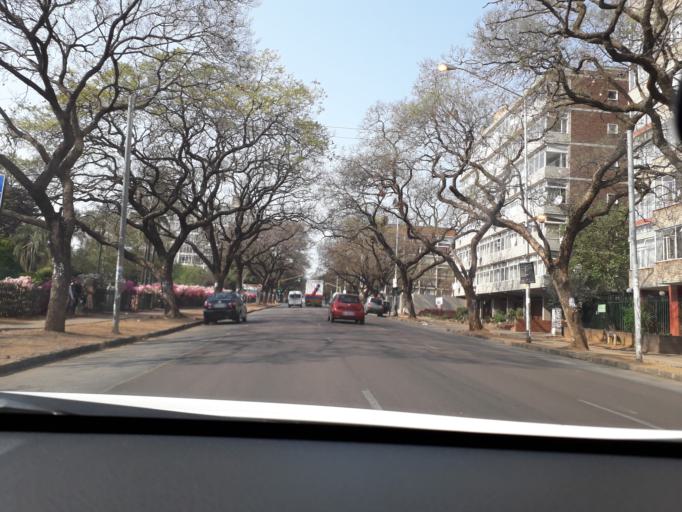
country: ZA
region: Gauteng
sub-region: City of Tshwane Metropolitan Municipality
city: Pretoria
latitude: -25.7539
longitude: 28.1912
